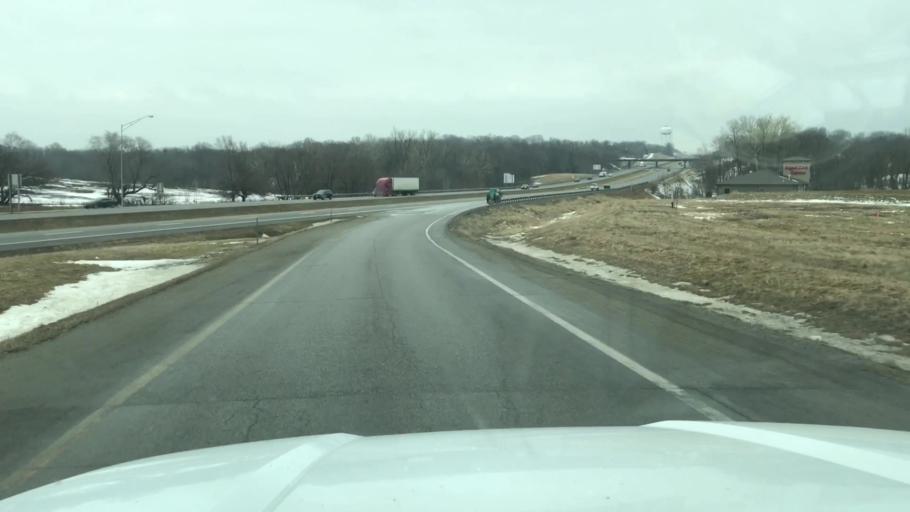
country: US
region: Missouri
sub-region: Andrew County
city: Country Club Village
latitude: 39.8123
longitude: -94.8035
